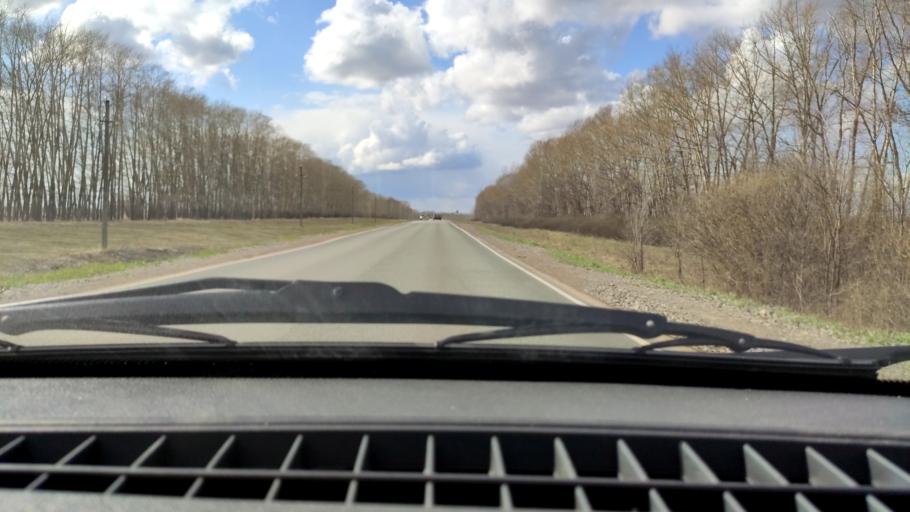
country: RU
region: Bashkortostan
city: Alekseyevka
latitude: 55.0609
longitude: 55.1058
